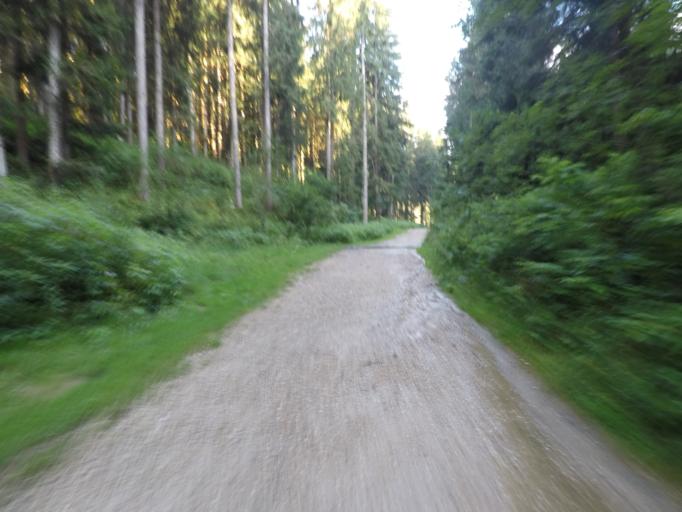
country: IT
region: Veneto
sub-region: Provincia di Vicenza
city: Asiago
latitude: 45.8596
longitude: 11.5277
